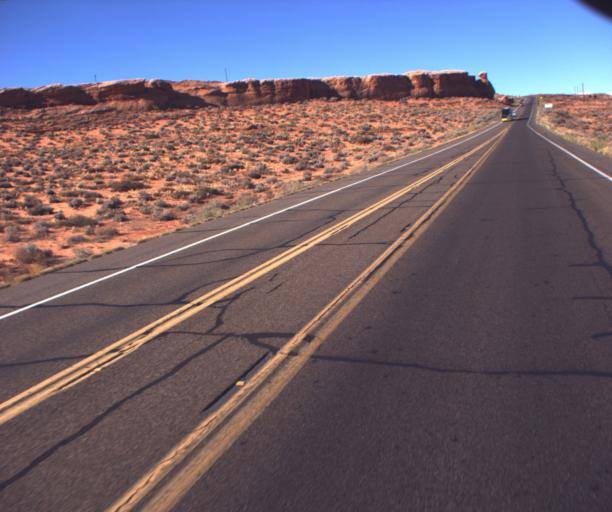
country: US
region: Arizona
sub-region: Coconino County
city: Page
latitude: 36.9414
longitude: -111.4953
